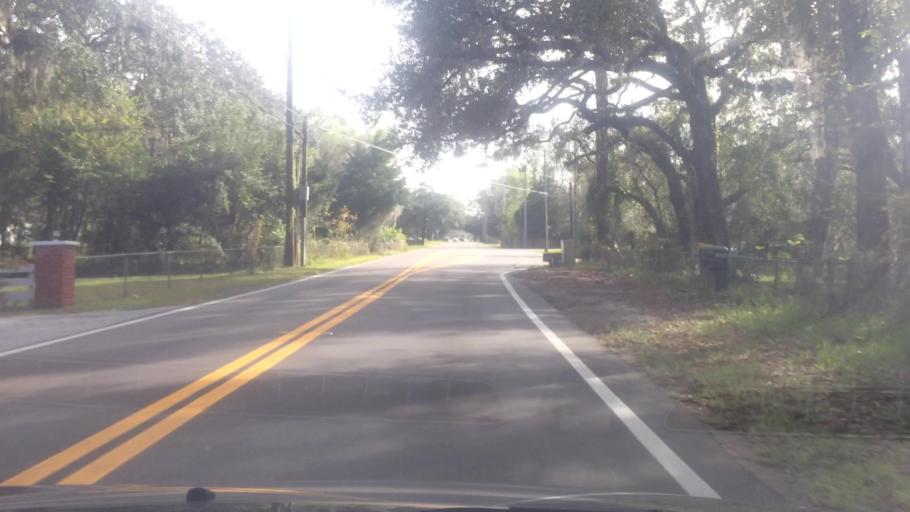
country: US
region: Florida
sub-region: Saint Johns County
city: Saint Augustine
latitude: 29.9209
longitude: -81.3608
